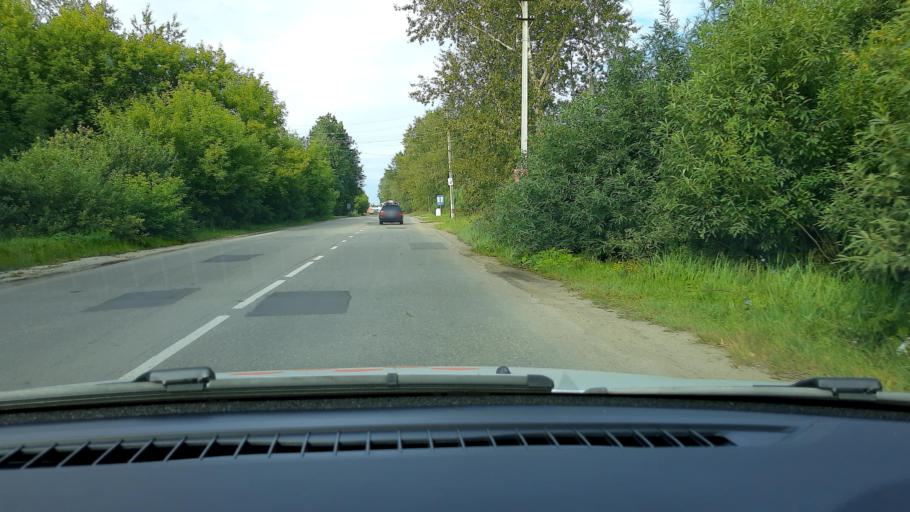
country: RU
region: Nizjnij Novgorod
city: Arzamas
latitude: 55.4188
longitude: 43.8471
